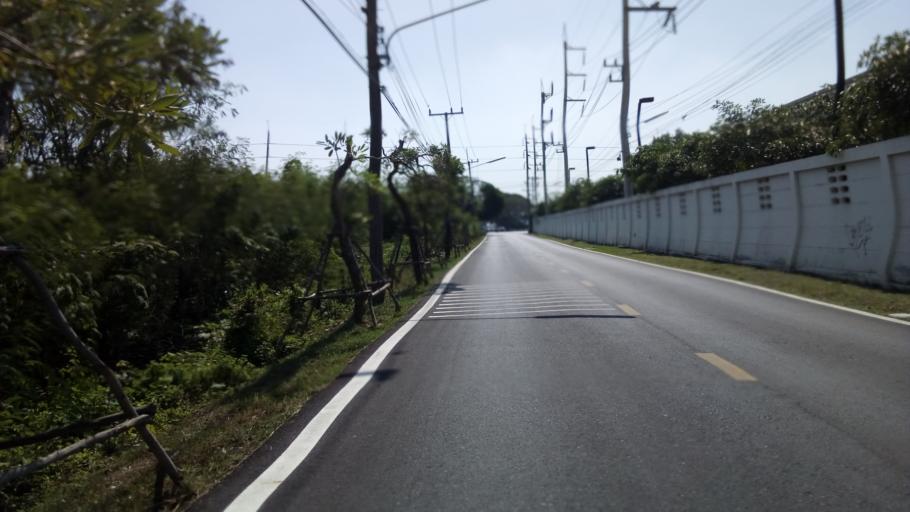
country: TH
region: Pathum Thani
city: Nong Suea
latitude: 14.0589
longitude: 100.8378
